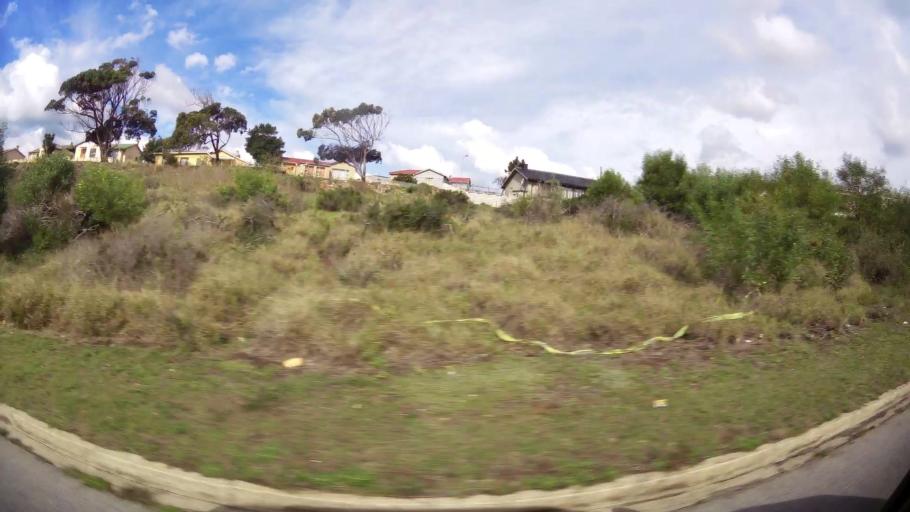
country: ZA
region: Eastern Cape
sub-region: Nelson Mandela Bay Metropolitan Municipality
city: Port Elizabeth
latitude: -33.9396
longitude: 25.5733
